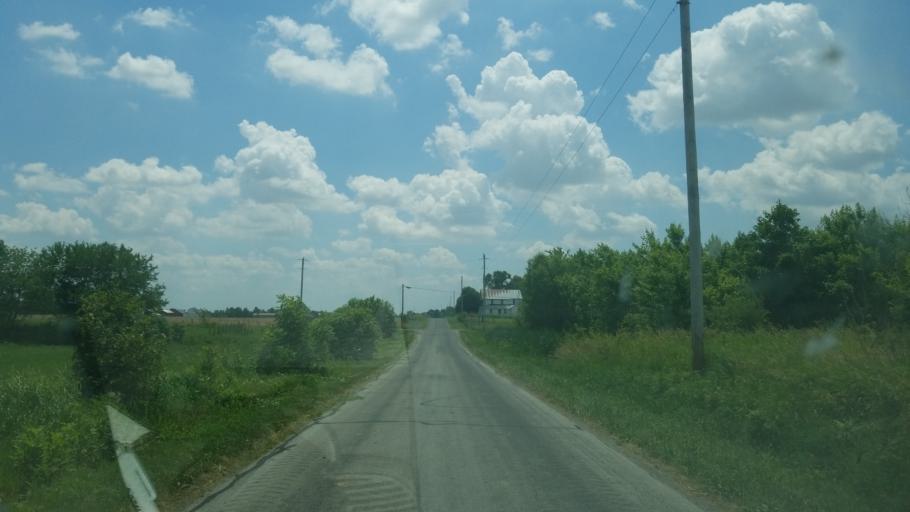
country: US
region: Ohio
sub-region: Hardin County
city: Kenton
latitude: 40.6144
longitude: -83.5589
